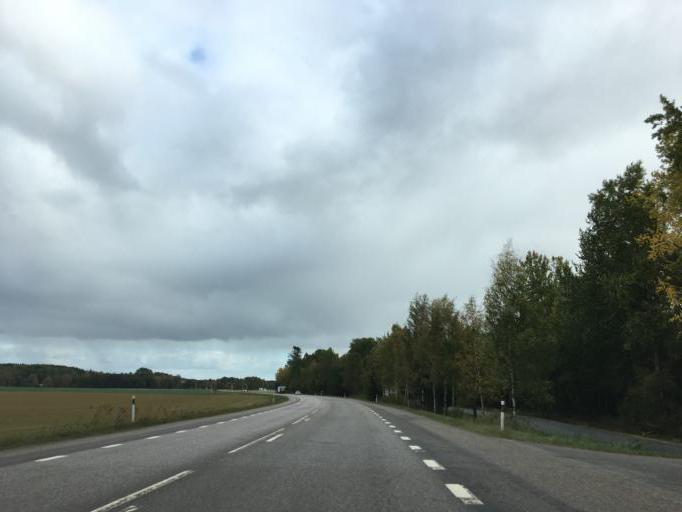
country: SE
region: Soedermanland
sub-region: Nykopings Kommun
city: Nykoping
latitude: 58.7704
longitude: 16.9350
